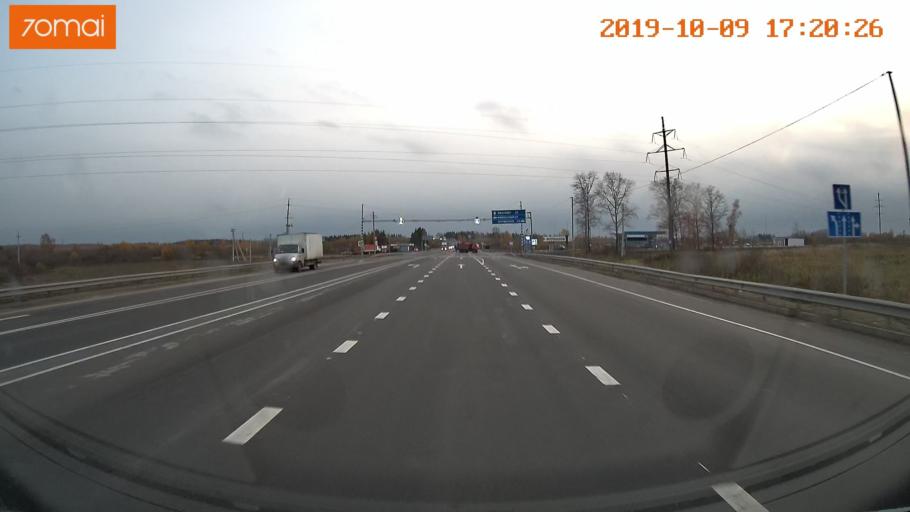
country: RU
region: Ivanovo
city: Furmanov
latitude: 57.2346
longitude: 41.1414
